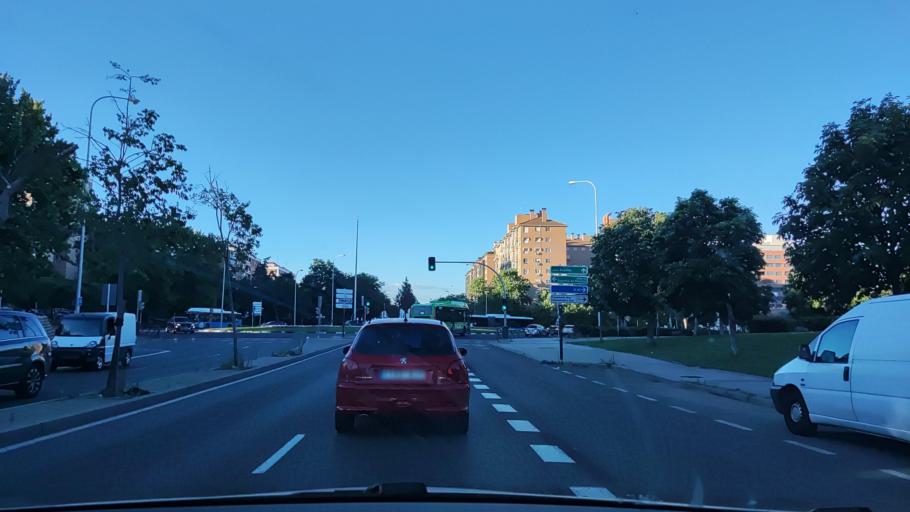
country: ES
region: Madrid
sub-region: Provincia de Madrid
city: Latina
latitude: 40.3730
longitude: -3.7348
